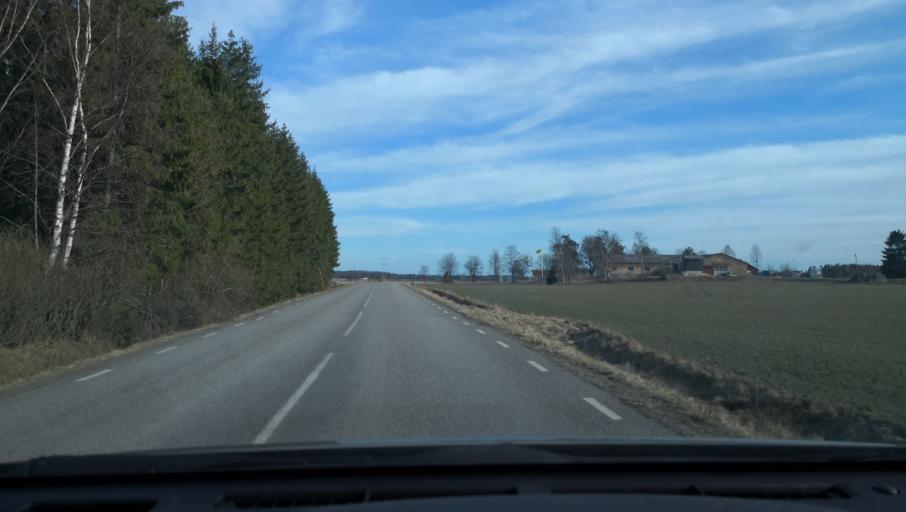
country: SE
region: Uppsala
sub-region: Enkopings Kommun
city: Enkoping
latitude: 59.6175
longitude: 17.1007
